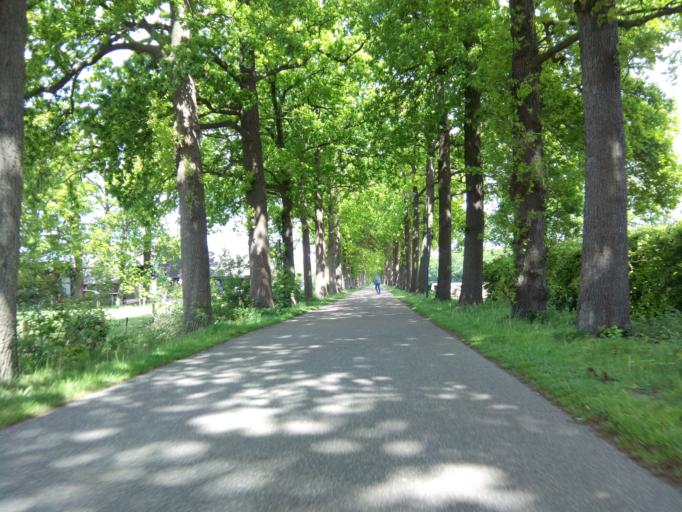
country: NL
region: Utrecht
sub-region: Gemeente Utrechtse Heuvelrug
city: Overberg
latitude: 52.0541
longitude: 5.4702
